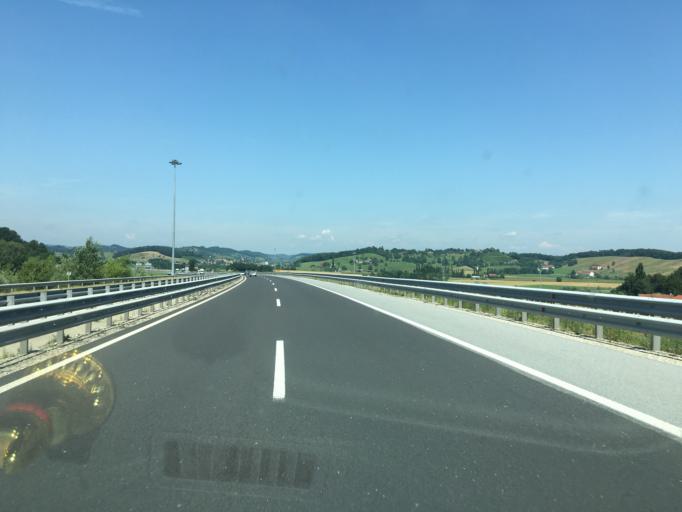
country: SI
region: Pesnica
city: Pesnica pri Mariboru
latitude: 46.5837
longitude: 15.6890
